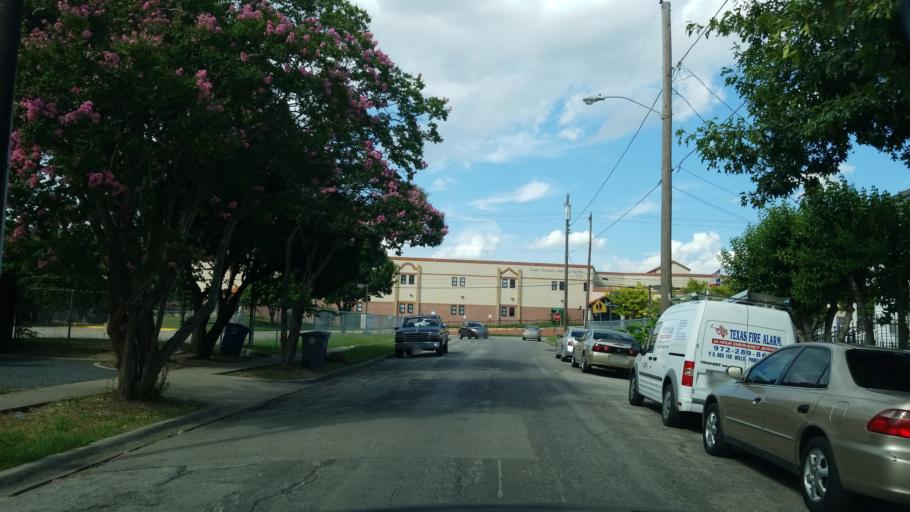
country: US
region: Texas
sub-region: Dallas County
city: Dallas
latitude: 32.8030
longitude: -96.7819
